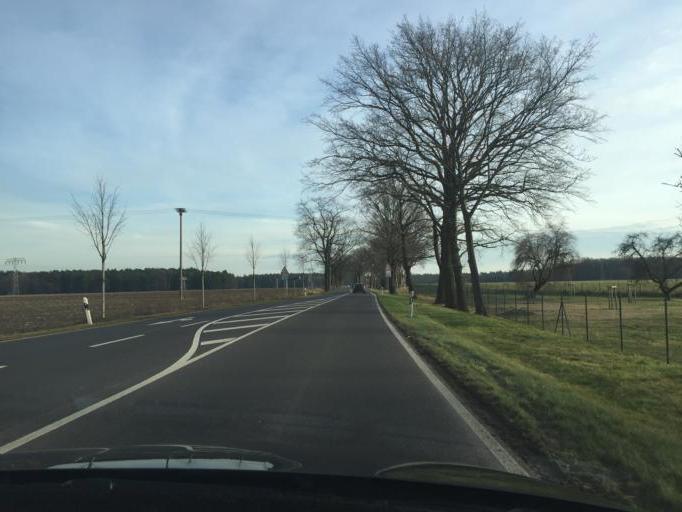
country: DE
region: Brandenburg
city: Cottbus
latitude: 51.7476
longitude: 14.3769
